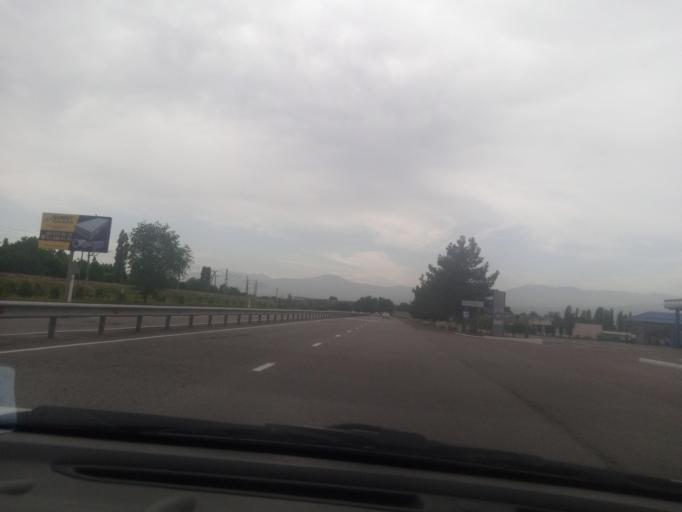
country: UZ
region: Toshkent
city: Ohangaron
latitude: 40.9085
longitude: 69.7926
